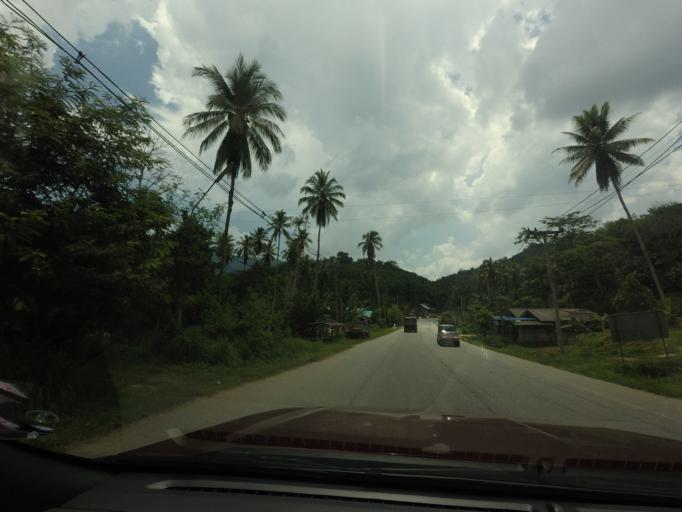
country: TH
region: Yala
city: Than To
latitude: 6.0729
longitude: 101.1927
